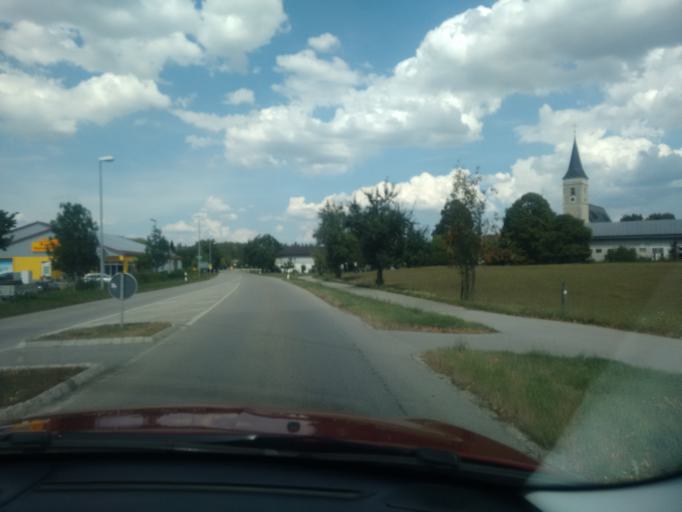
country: DE
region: Bavaria
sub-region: Upper Bavaria
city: Trostberg an der Alz
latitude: 48.0368
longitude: 12.5724
